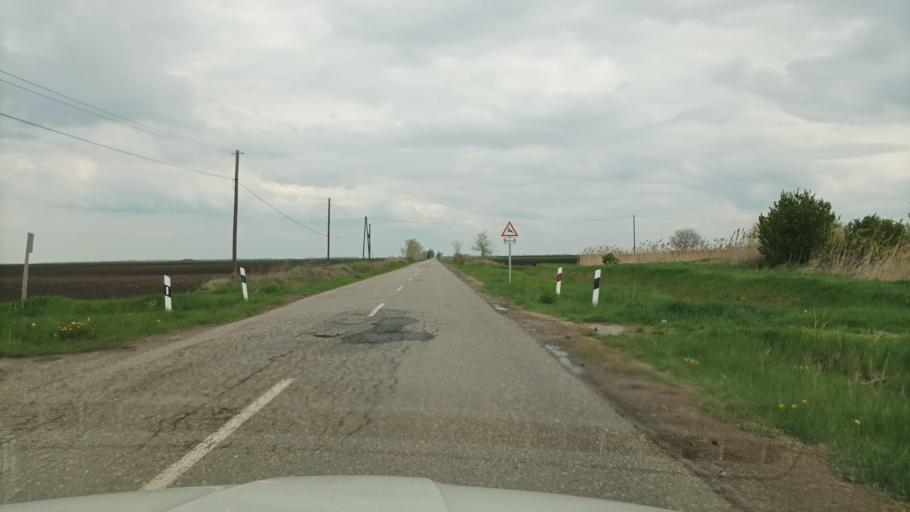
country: HU
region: Pest
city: Tortel
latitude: 47.1260
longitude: 19.9437
